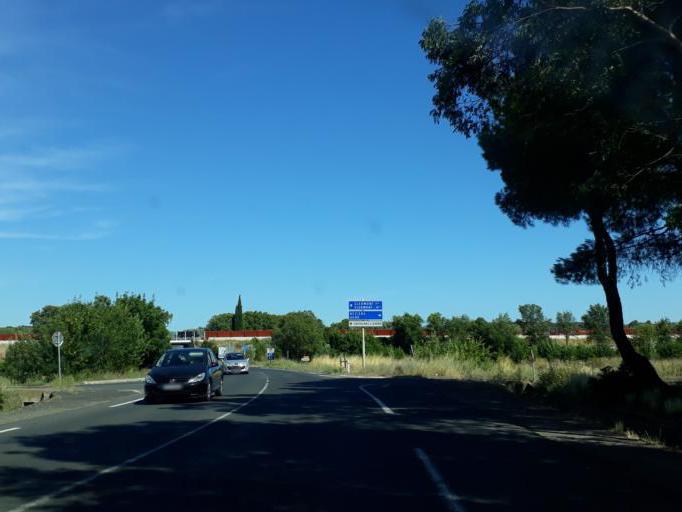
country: FR
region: Languedoc-Roussillon
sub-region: Departement de l'Herault
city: Pezenas
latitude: 43.4532
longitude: 3.4277
